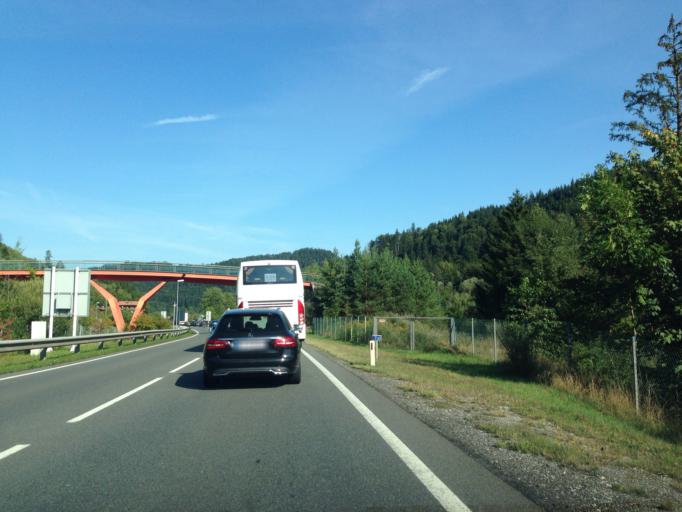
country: AT
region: Tyrol
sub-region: Politischer Bezirk Reutte
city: Musau
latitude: 47.5421
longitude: 10.6654
